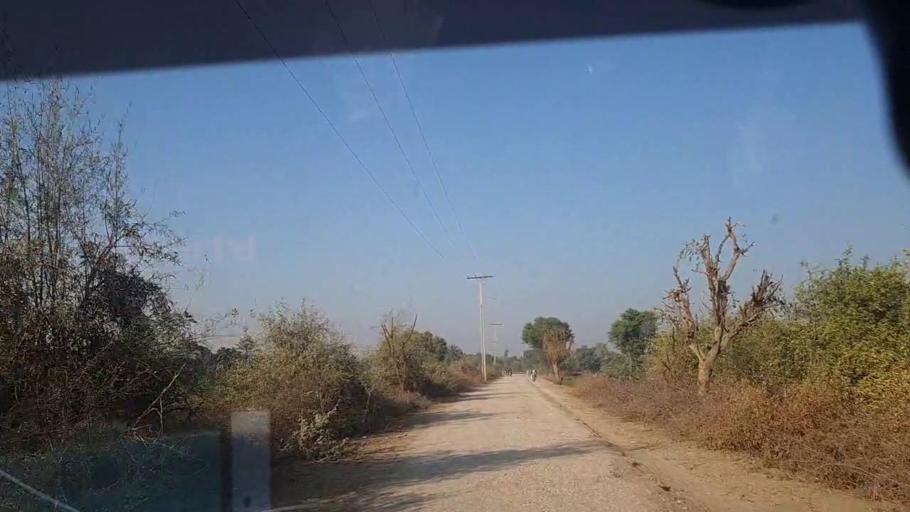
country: PK
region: Sindh
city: Sobhadero
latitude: 27.2511
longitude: 68.3502
